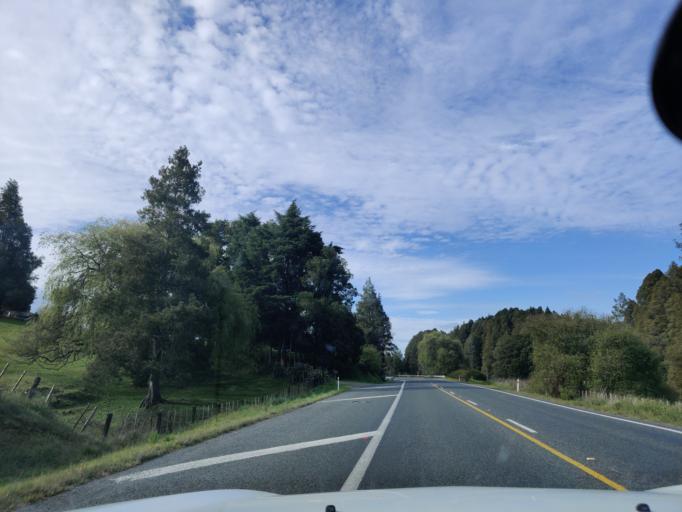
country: NZ
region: Waikato
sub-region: Otorohanga District
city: Otorohanga
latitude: -38.2829
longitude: 175.1546
